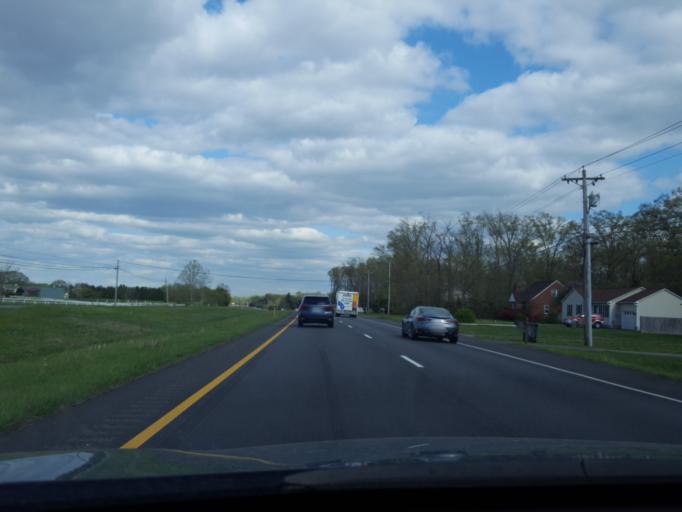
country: US
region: Maryland
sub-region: Charles County
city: Hughesville
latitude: 38.5515
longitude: -76.8283
